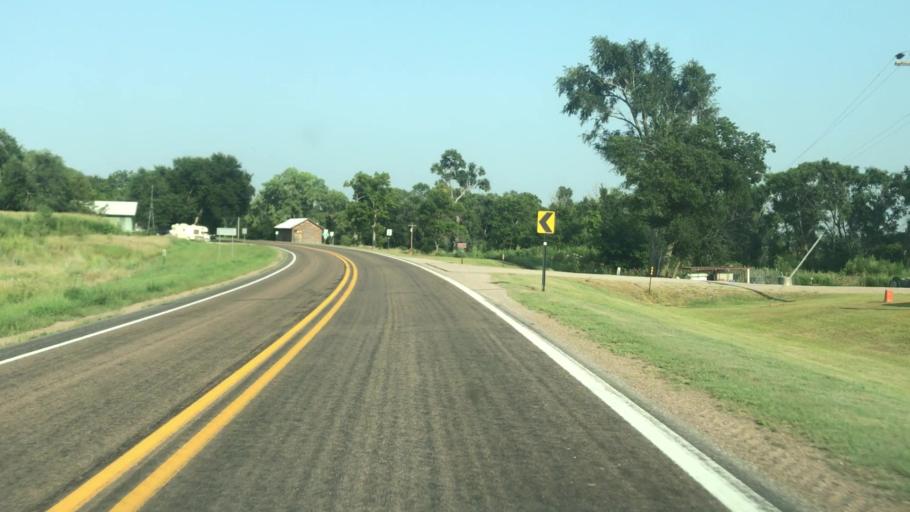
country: US
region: Nebraska
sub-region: Buffalo County
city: Ravenna
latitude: 41.0742
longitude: -98.7249
